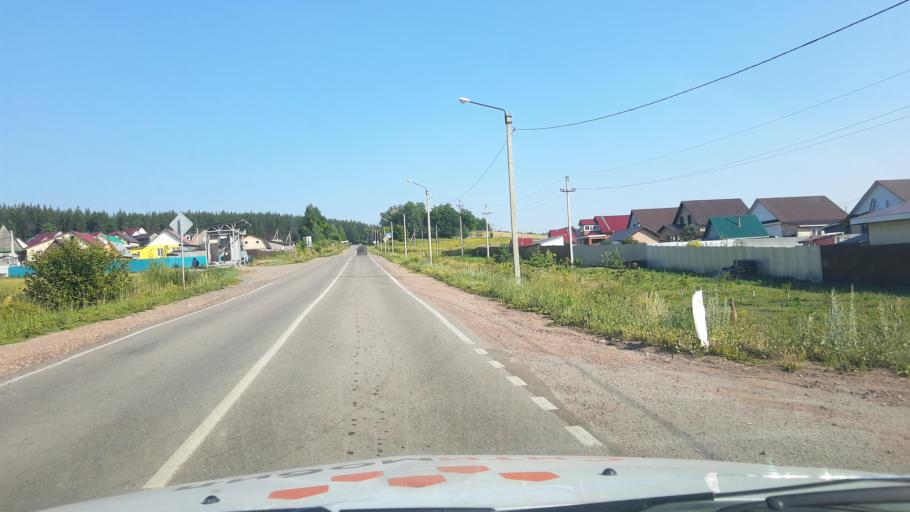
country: RU
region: Bashkortostan
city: Avdon
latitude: 54.6325
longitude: 55.6146
